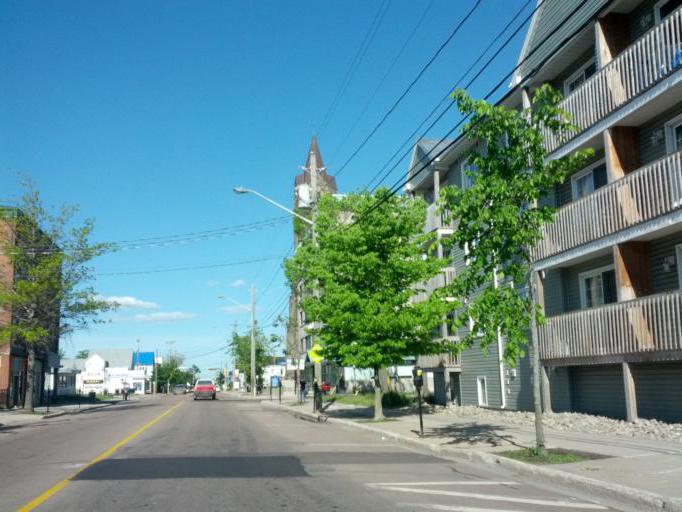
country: CA
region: New Brunswick
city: Moncton
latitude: 46.0909
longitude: -64.7840
